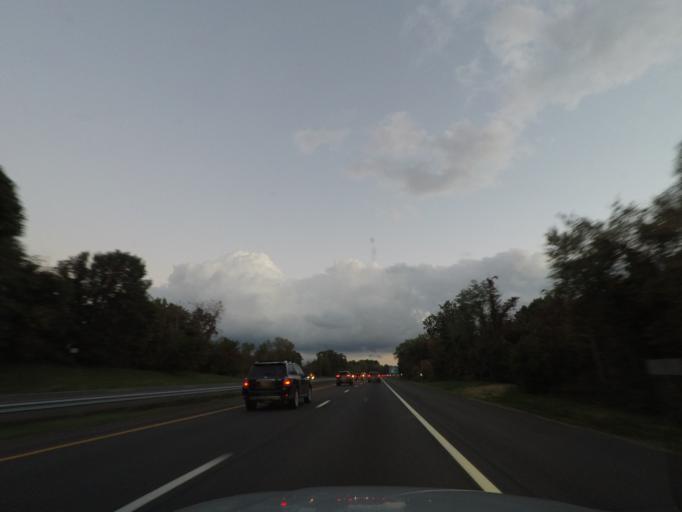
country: US
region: New York
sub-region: Ulster County
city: Clintondale
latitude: 41.6709
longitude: -74.0795
